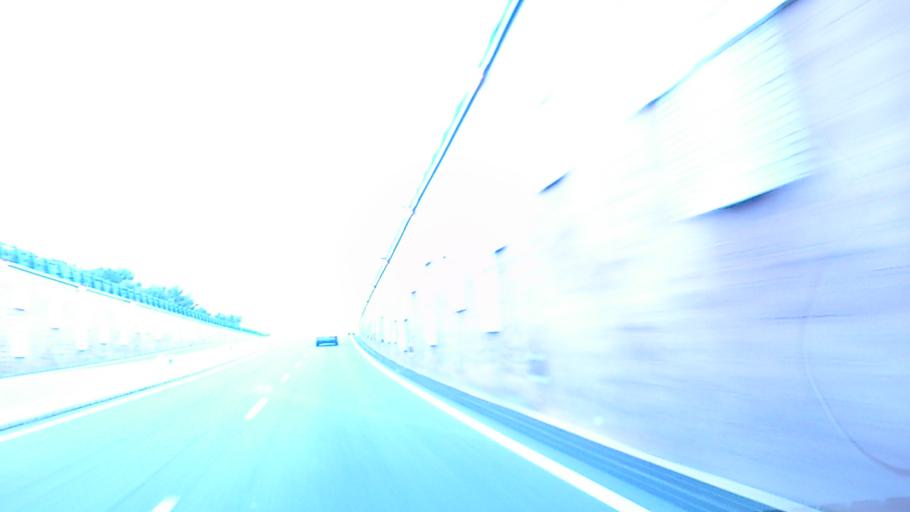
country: ES
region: Aragon
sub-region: Provincia de Zaragoza
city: Zaragoza
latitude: 41.6891
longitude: -0.8713
